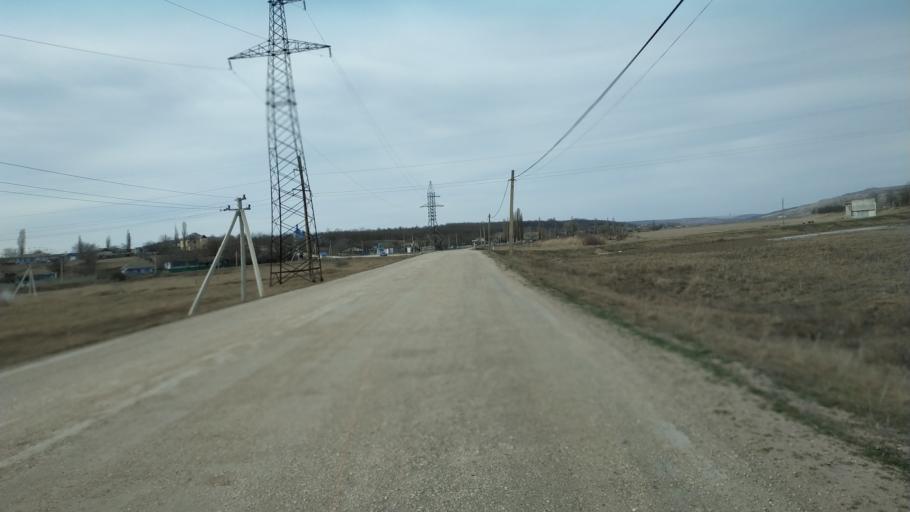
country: RO
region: Vaslui
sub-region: Comuna Dranceni
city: Dranceni
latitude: 46.8584
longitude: 28.2047
